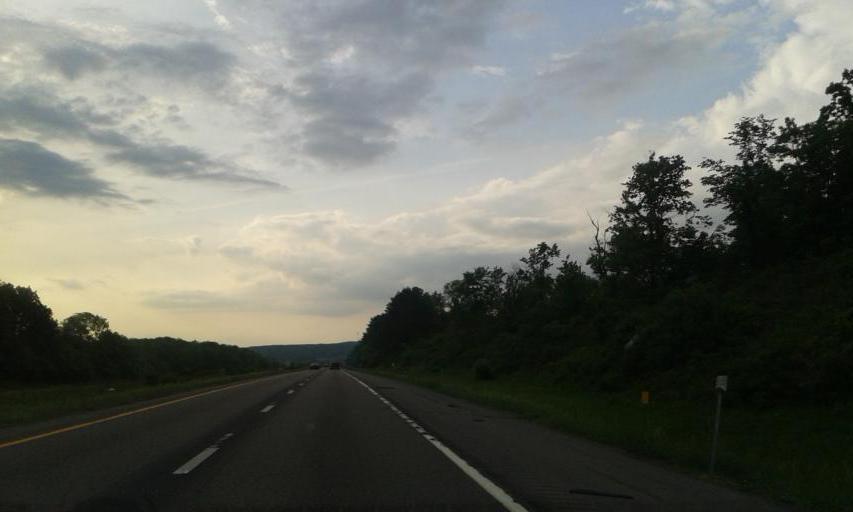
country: US
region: New York
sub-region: Broome County
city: Chenango Bridge
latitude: 42.0788
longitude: -75.8035
